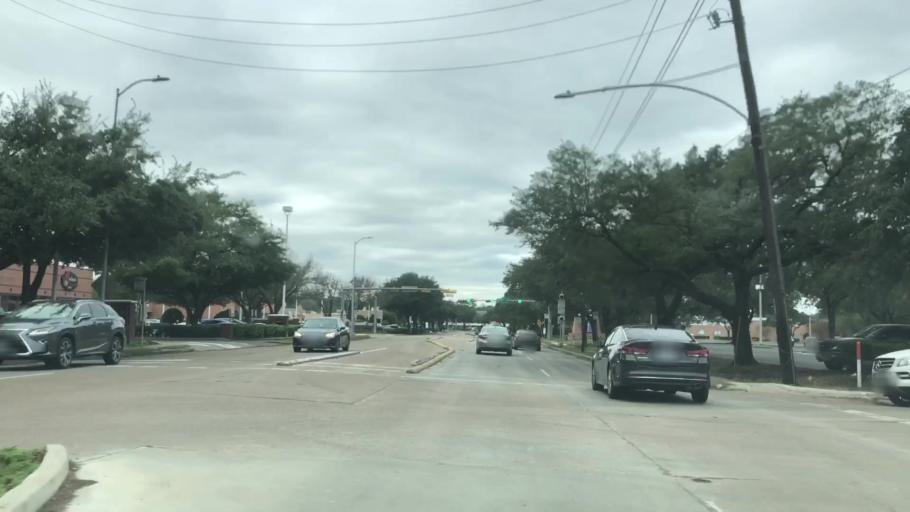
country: US
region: Texas
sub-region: Harris County
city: Hunters Creek Village
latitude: 29.7560
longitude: -95.4969
